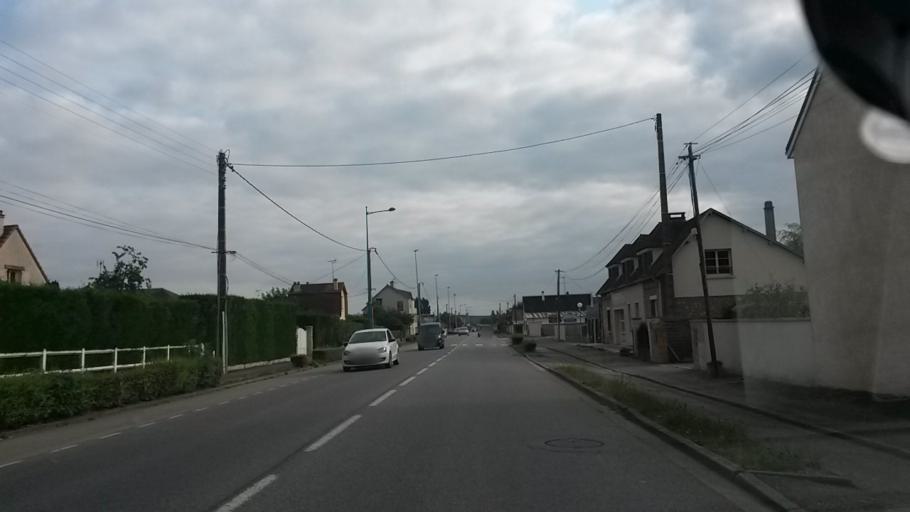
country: FR
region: Haute-Normandie
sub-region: Departement de l'Eure
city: Gravigny
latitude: 49.0533
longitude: 1.1662
